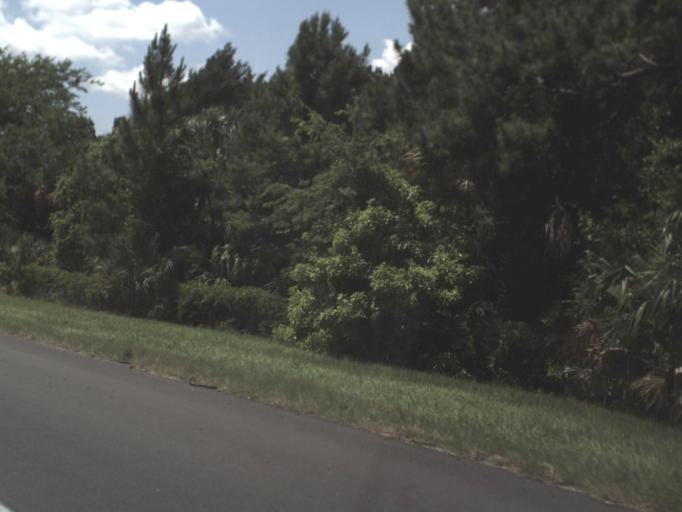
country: US
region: Florida
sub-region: Nassau County
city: Yulee
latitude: 30.5776
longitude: -81.6465
